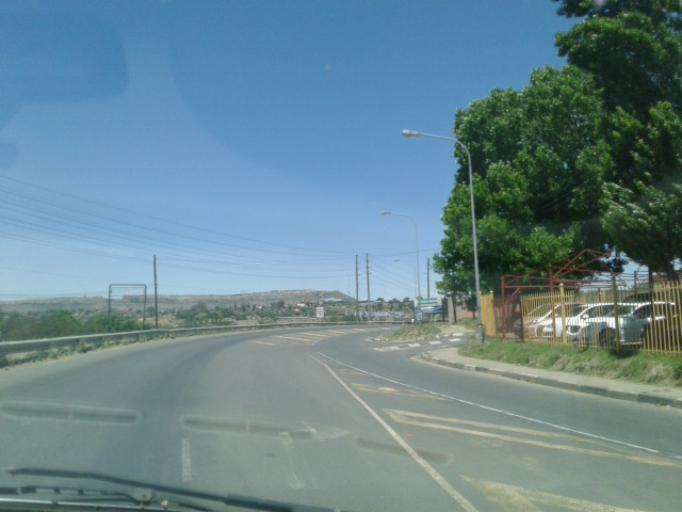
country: LS
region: Maseru
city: Maseru
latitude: -29.2987
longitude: 27.4798
